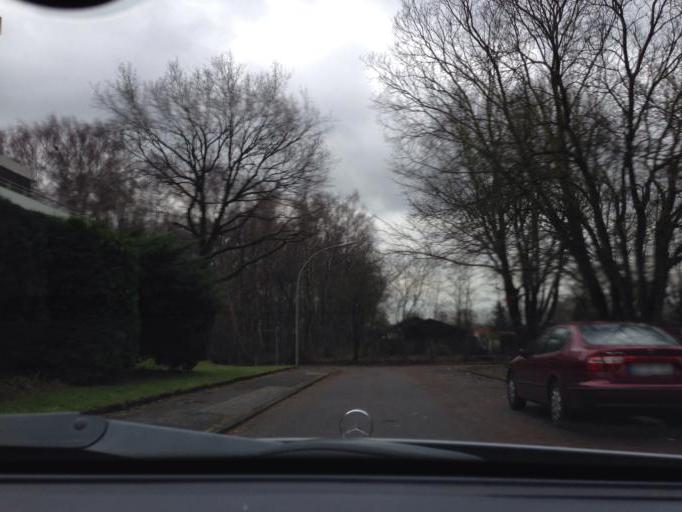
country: DE
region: Schleswig-Holstein
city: Barsbuettel
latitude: 53.5864
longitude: 10.1726
